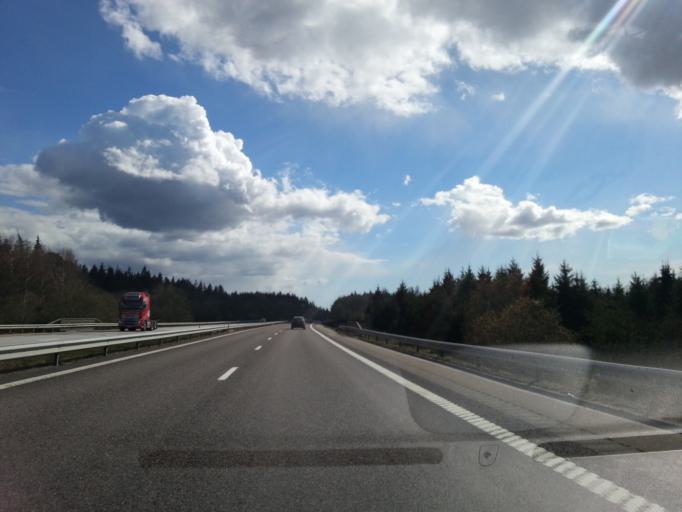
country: SE
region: Vaestra Goetaland
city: Svanesund
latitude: 58.1343
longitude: 11.8857
